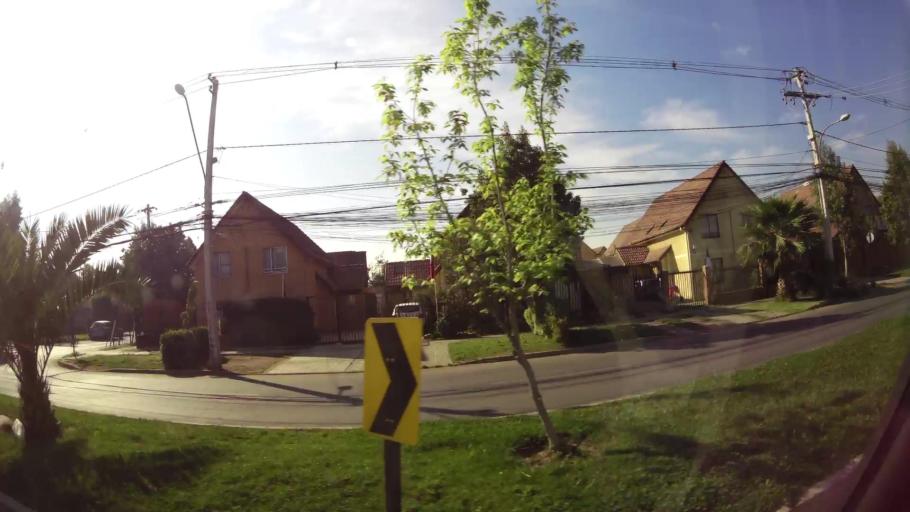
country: CL
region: Santiago Metropolitan
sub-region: Provincia de Santiago
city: Lo Prado
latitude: -33.4529
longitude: -70.7569
